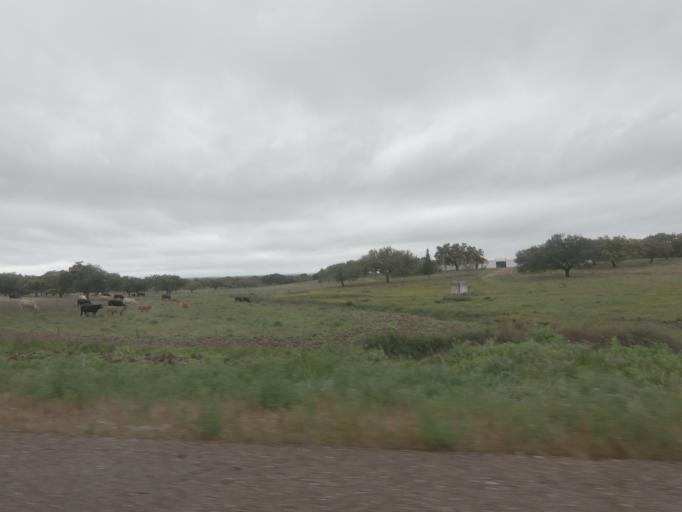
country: ES
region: Extremadura
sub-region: Provincia de Badajoz
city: Villar del Rey
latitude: 39.0439
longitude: -6.8076
